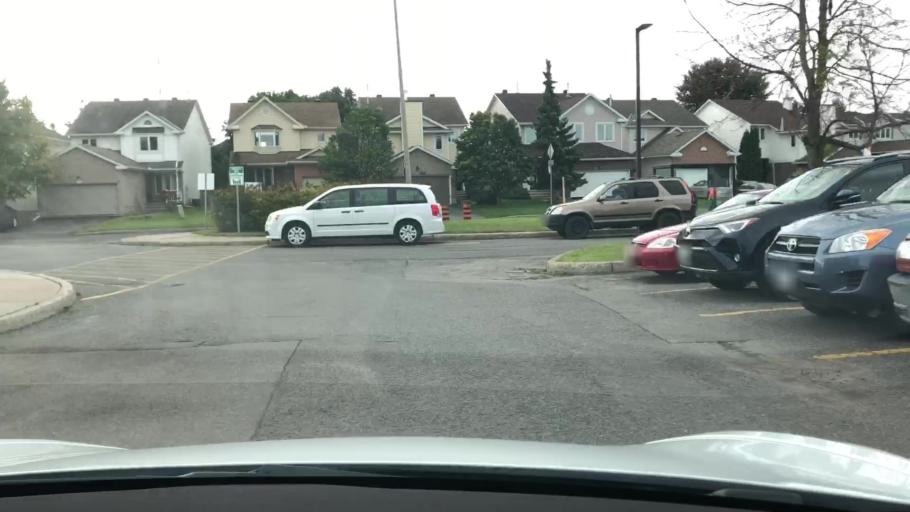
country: CA
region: Ontario
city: Clarence-Rockland
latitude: 45.4689
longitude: -75.4750
